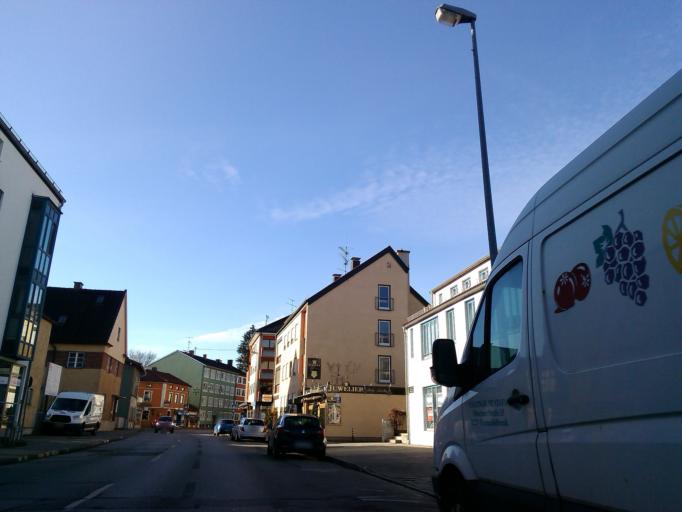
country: DE
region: Bavaria
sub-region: Upper Bavaria
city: Fuerstenfeldbruck
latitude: 48.1765
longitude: 11.2586
